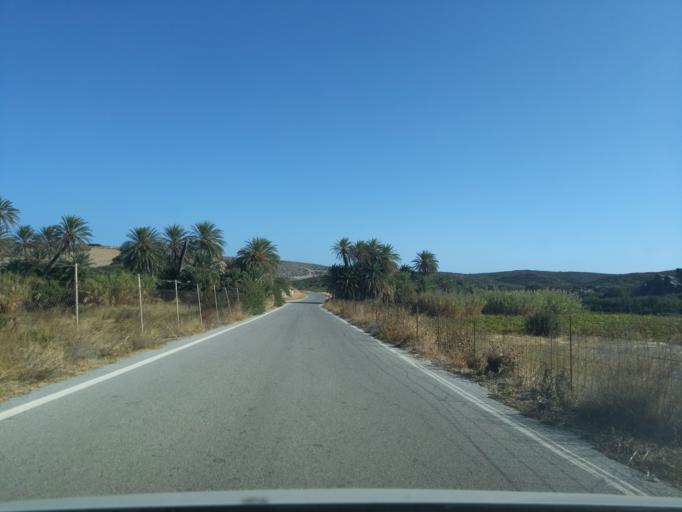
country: GR
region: Crete
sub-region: Nomos Lasithiou
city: Palekastro
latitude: 35.2508
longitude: 26.2516
